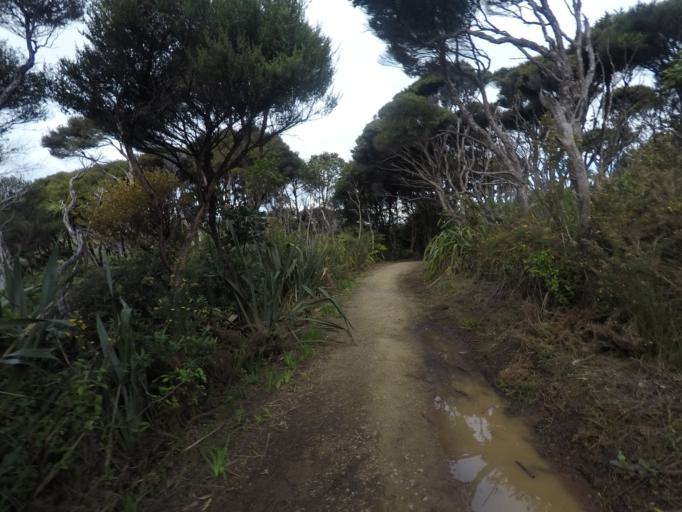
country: NZ
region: Auckland
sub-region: Auckland
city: Muriwai Beach
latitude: -36.9750
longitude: 174.4731
